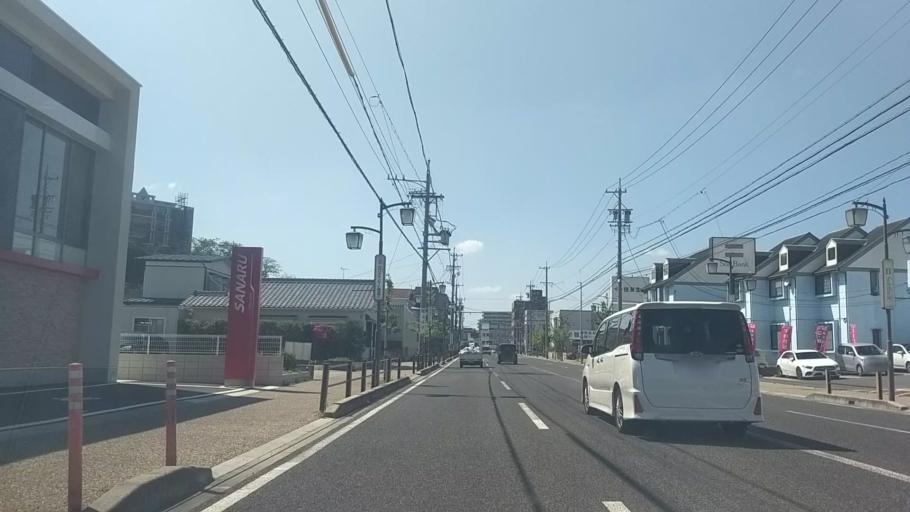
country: JP
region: Aichi
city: Okazaki
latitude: 34.9703
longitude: 137.1732
